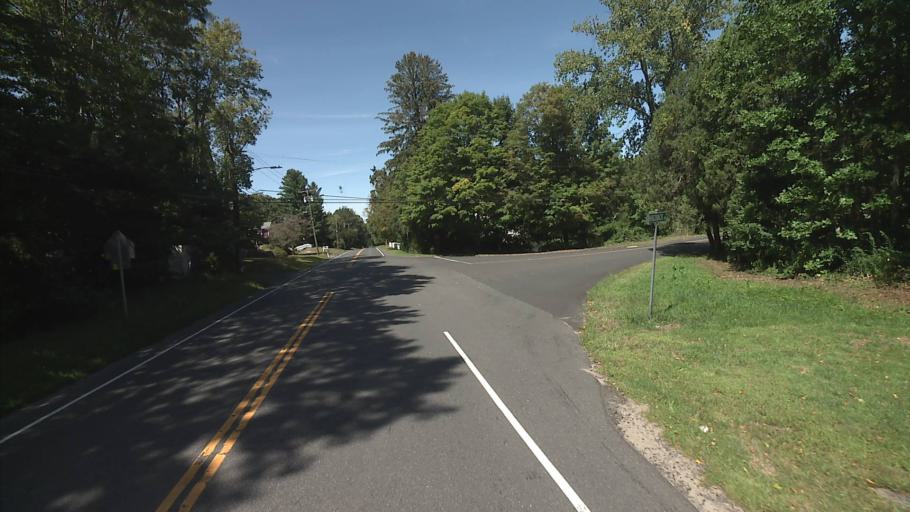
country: US
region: Connecticut
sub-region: New Haven County
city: Oxford
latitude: 41.4274
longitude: -73.1562
